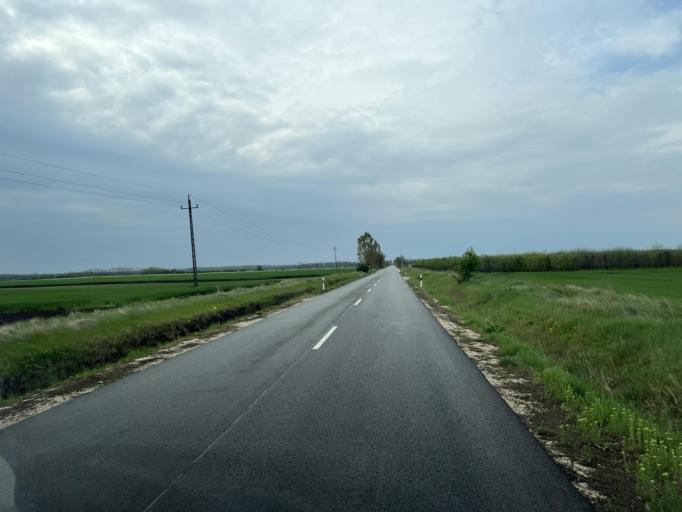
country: HU
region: Pest
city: Nyaregyhaza
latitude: 47.2516
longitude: 19.5217
